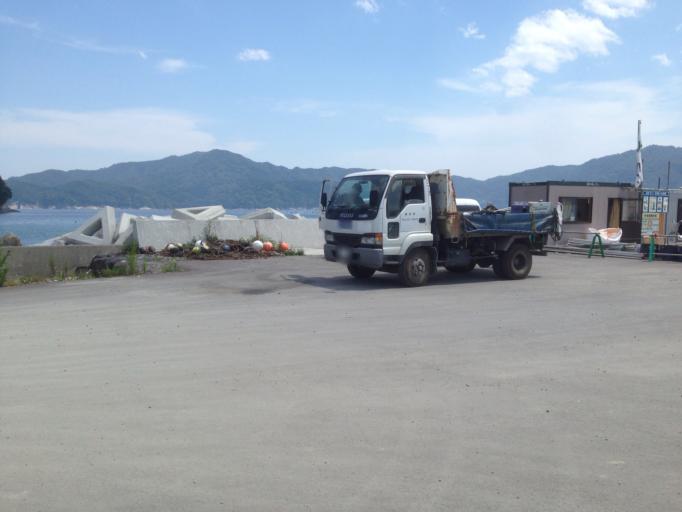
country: JP
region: Iwate
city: Otsuchi
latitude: 39.3510
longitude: 141.9340
